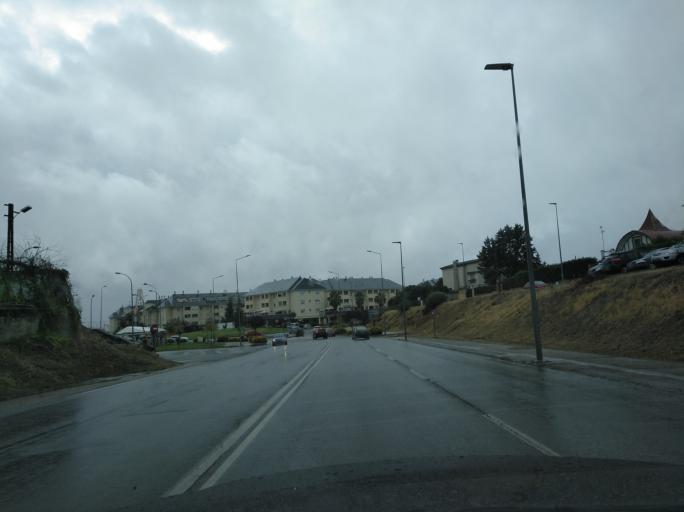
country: ES
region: Extremadura
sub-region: Provincia de Badajoz
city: Badajoz
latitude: 38.8846
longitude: -6.9907
